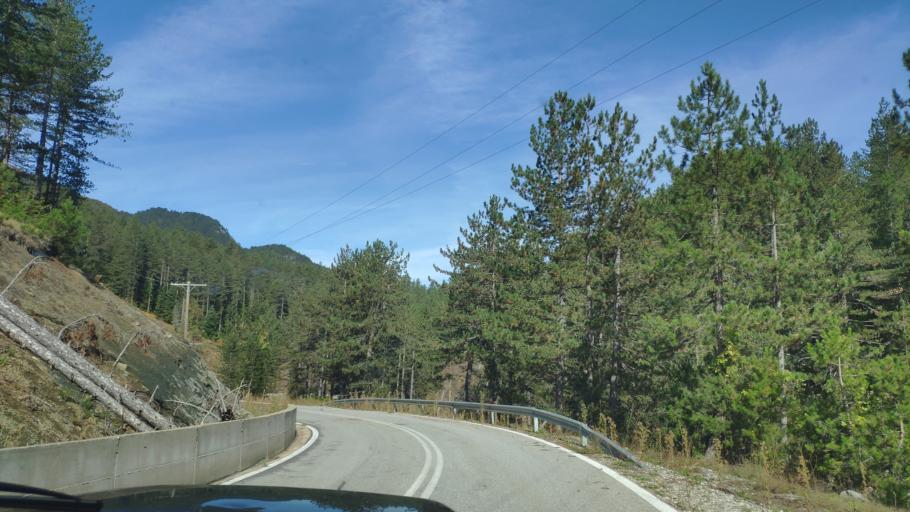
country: AL
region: Korce
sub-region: Rrethi i Devollit
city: Miras
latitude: 40.4045
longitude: 20.8791
